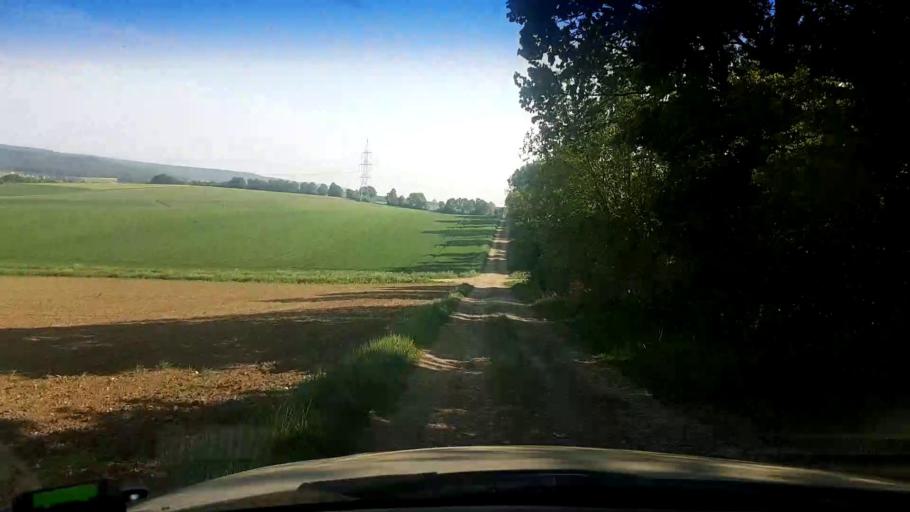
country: DE
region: Bavaria
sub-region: Upper Franconia
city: Memmelsdorf
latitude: 49.9644
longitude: 10.9763
